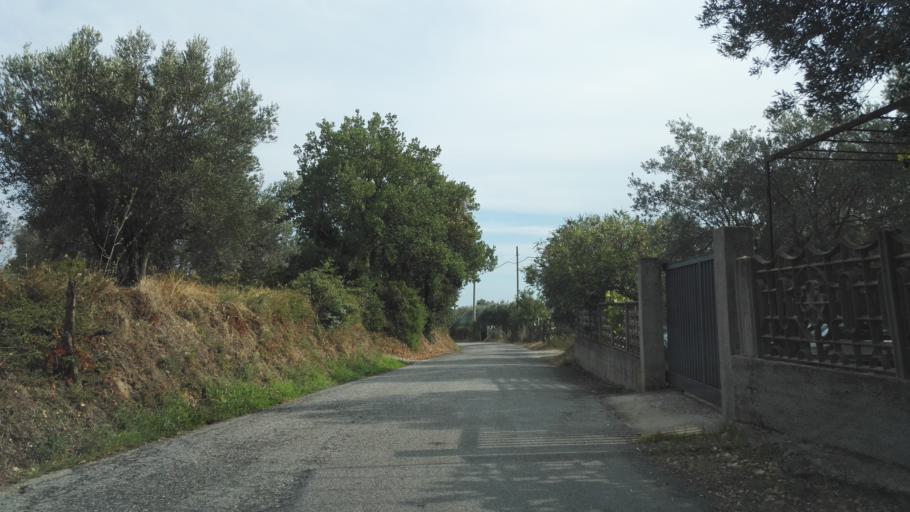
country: IT
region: Calabria
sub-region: Provincia di Reggio Calabria
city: Stignano
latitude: 38.4256
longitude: 16.4650
